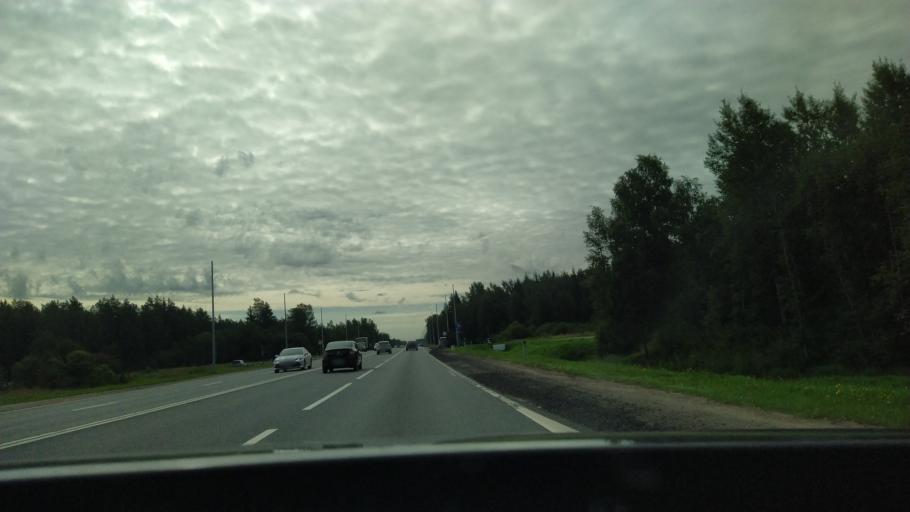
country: RU
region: Leningrad
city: Ul'yanovka
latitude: 59.5797
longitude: 30.8066
